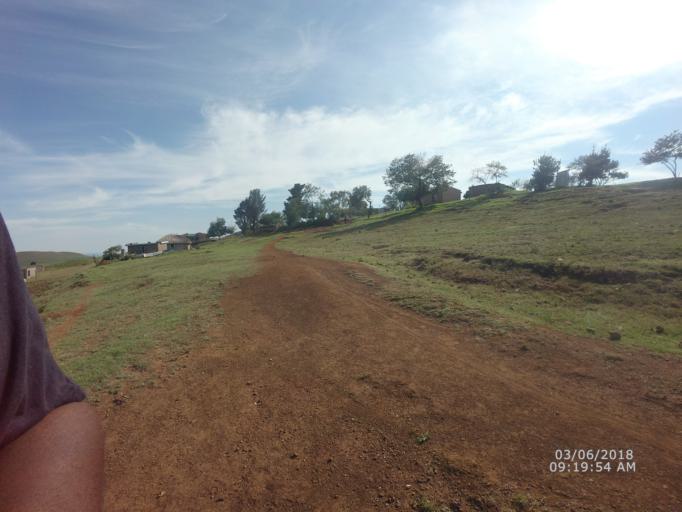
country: LS
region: Berea
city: Teyateyaneng
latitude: -29.2284
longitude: 27.8646
